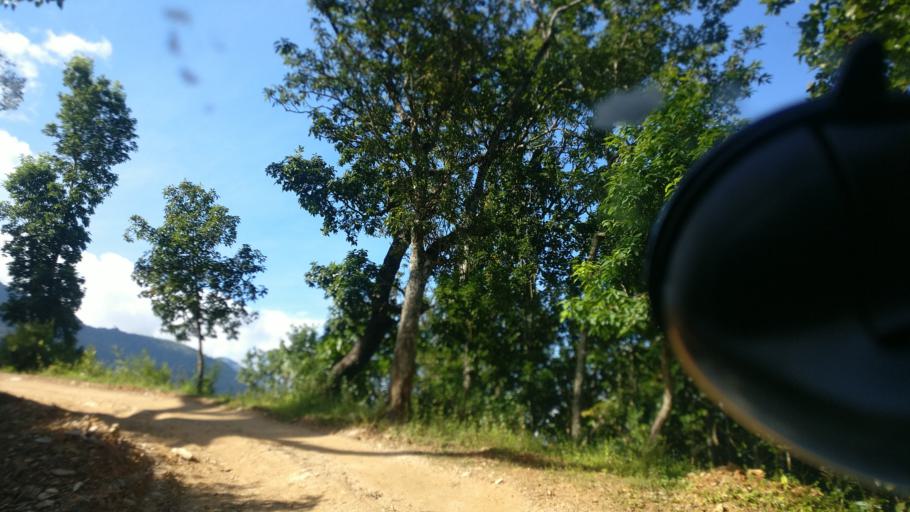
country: NP
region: Western Region
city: Baglung
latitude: 28.1373
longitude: 83.6468
